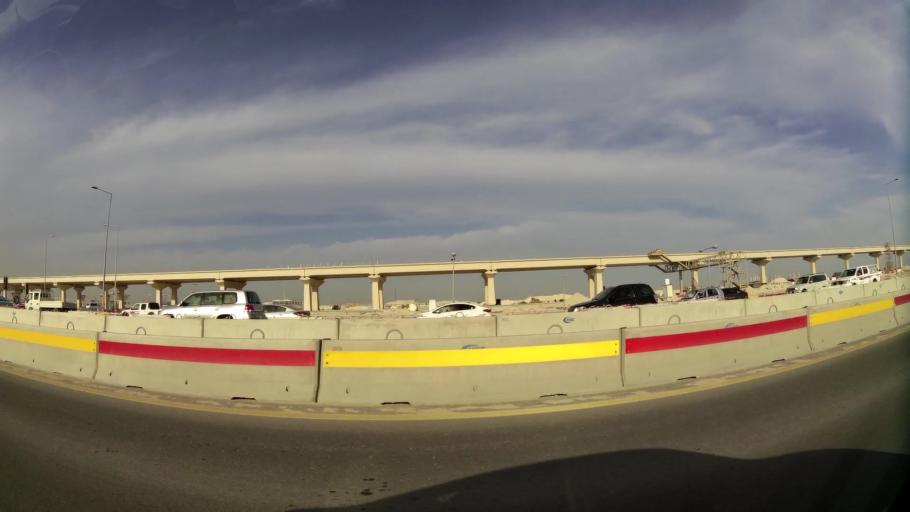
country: QA
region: Al Wakrah
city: Al Wakrah
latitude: 25.2056
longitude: 51.5882
